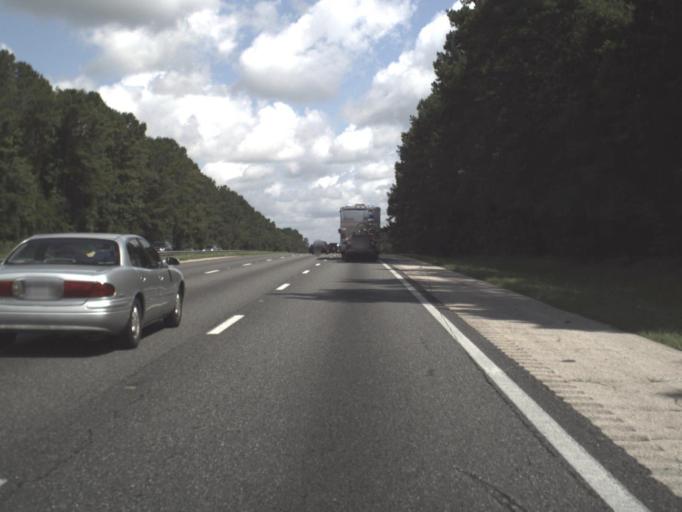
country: US
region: Florida
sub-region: Alachua County
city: High Springs
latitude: 29.8181
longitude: -82.5161
